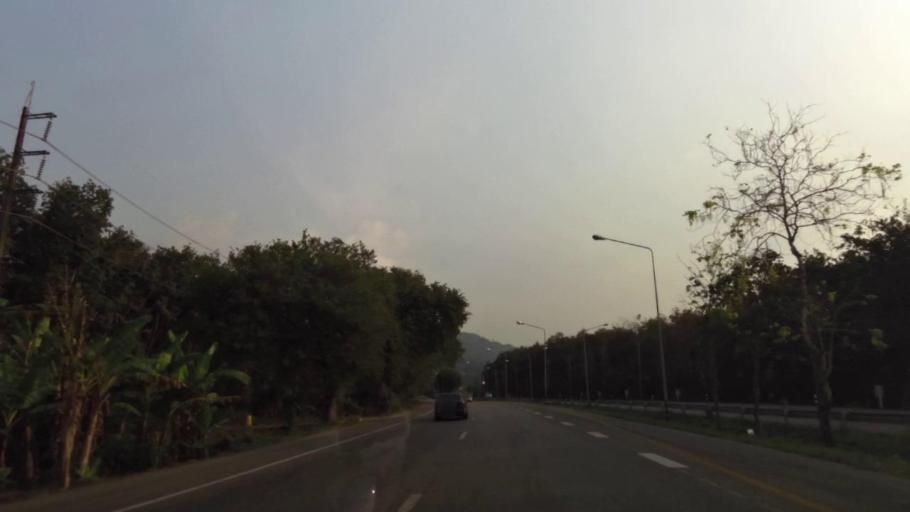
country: TH
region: Chanthaburi
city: Chanthaburi
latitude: 12.5771
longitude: 102.1603
